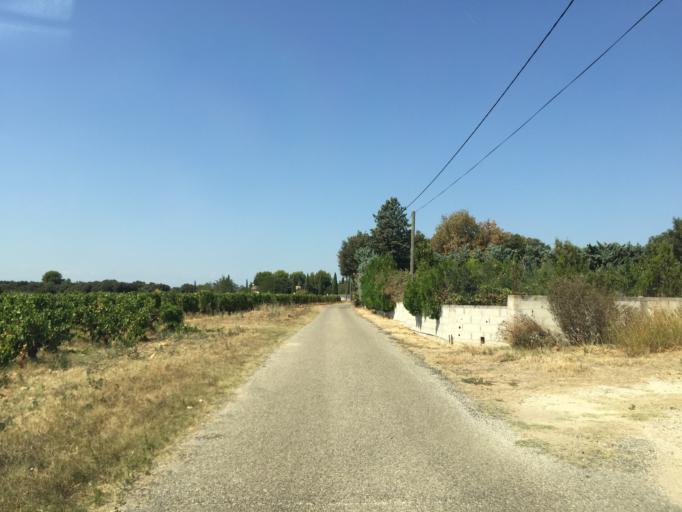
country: FR
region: Provence-Alpes-Cote d'Azur
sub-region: Departement du Vaucluse
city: Orange
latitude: 44.1125
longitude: 4.8135
